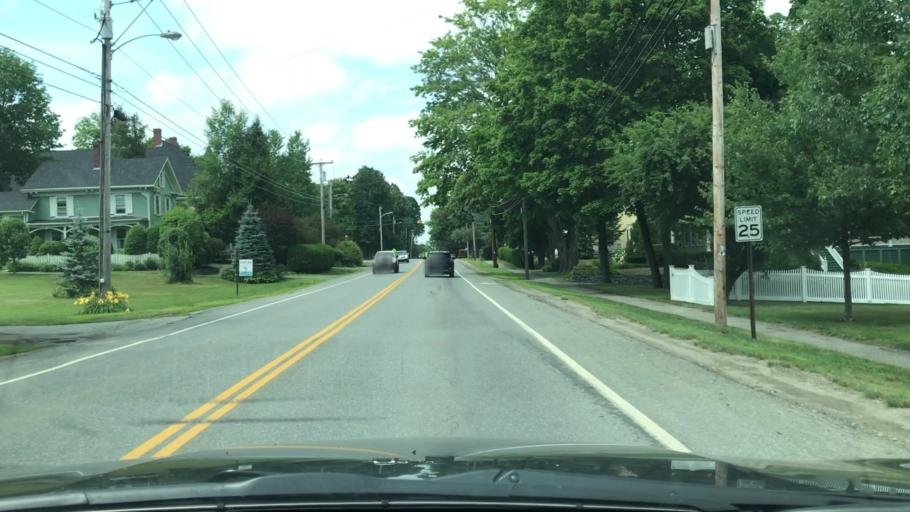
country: US
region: Maine
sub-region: Waldo County
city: Belfast
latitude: 44.4192
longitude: -68.9988
